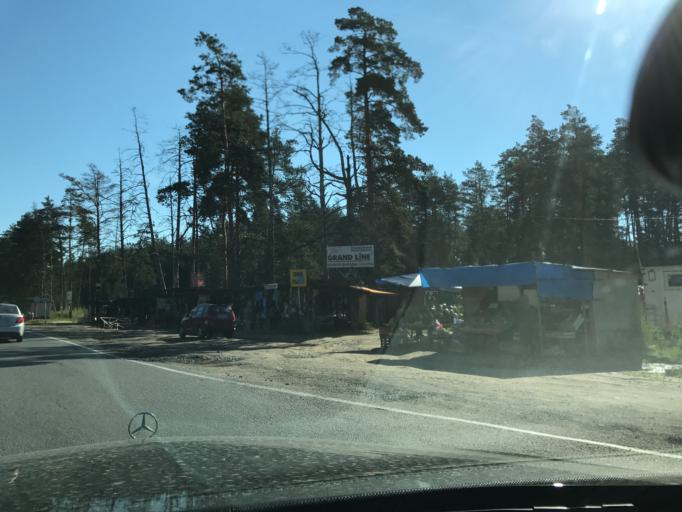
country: RU
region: Moskovskaya
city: Noginsk-9
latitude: 56.0939
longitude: 38.6747
